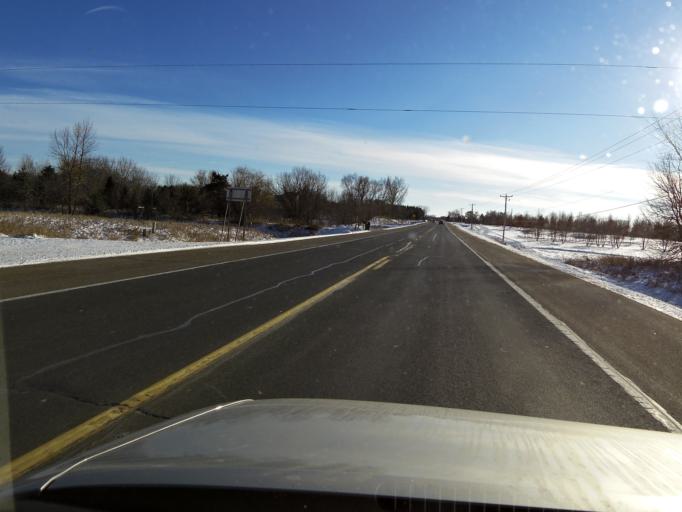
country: US
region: Minnesota
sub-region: Washington County
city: Lake Elmo
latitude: 44.9913
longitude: -92.8629
